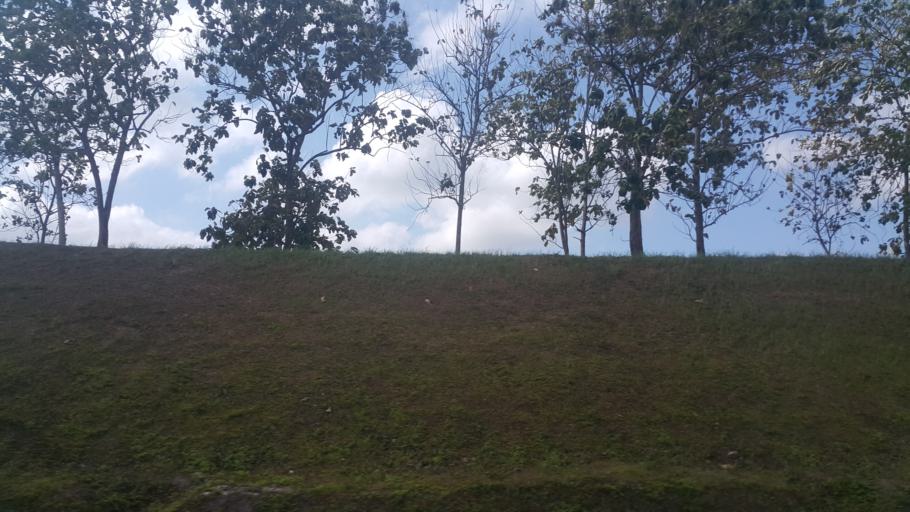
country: MY
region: Johor
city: Yong Peng
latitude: 1.9962
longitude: 103.0720
